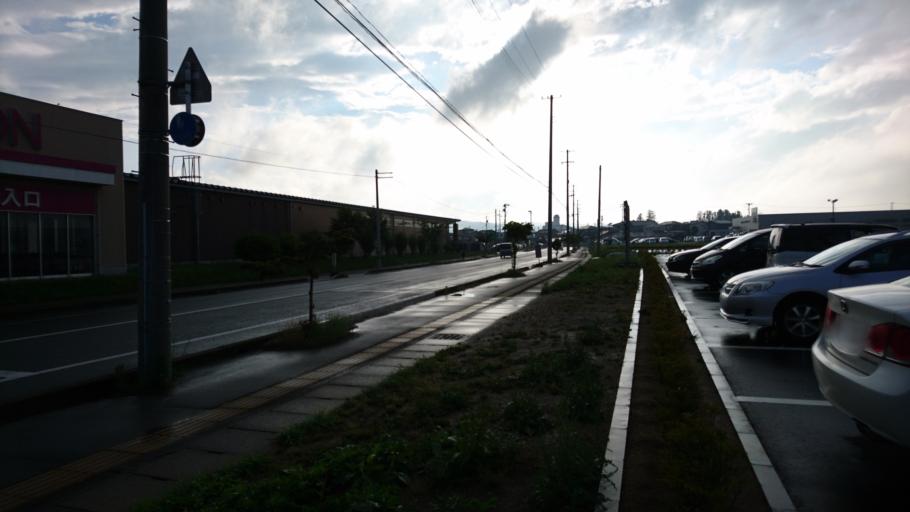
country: JP
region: Iwate
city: Ichinoseki
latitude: 38.9402
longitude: 141.1541
